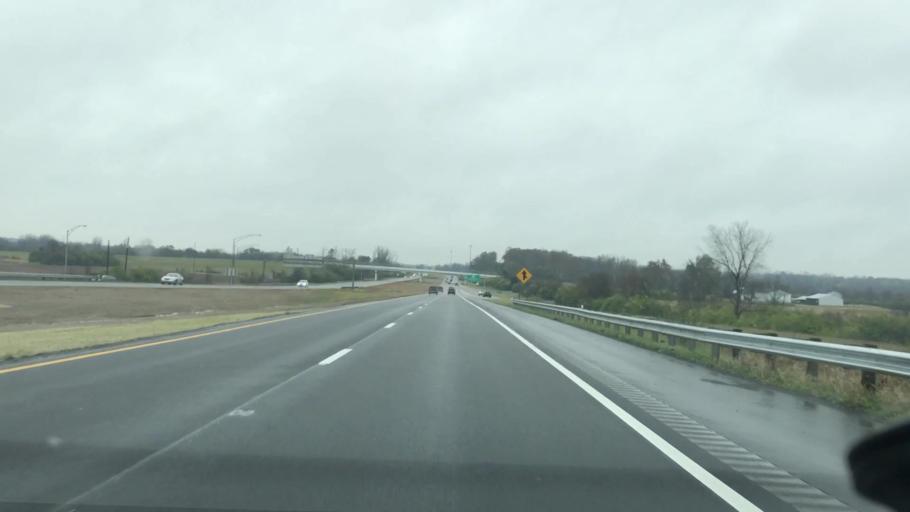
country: US
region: Ohio
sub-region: Clark County
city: Holiday Valley
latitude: 39.8628
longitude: -83.9941
